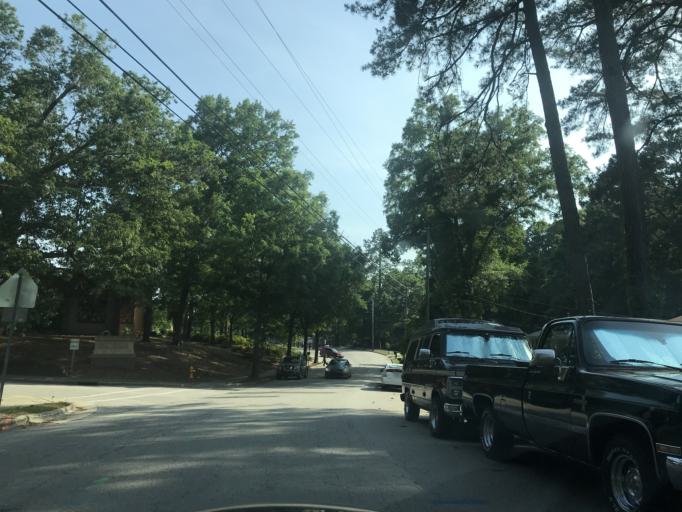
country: US
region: North Carolina
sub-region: Wake County
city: Raleigh
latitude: 35.7667
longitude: -78.5864
